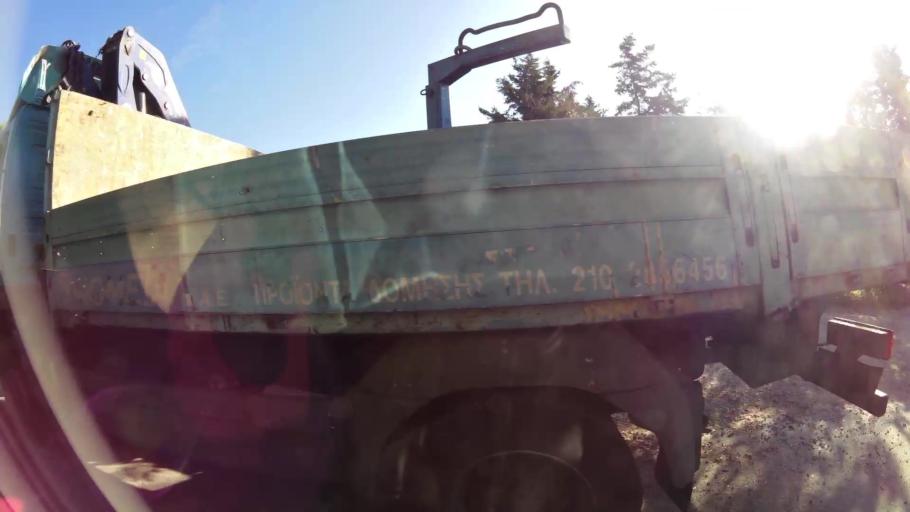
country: GR
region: Attica
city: Pefki
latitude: 38.0532
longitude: 23.7831
